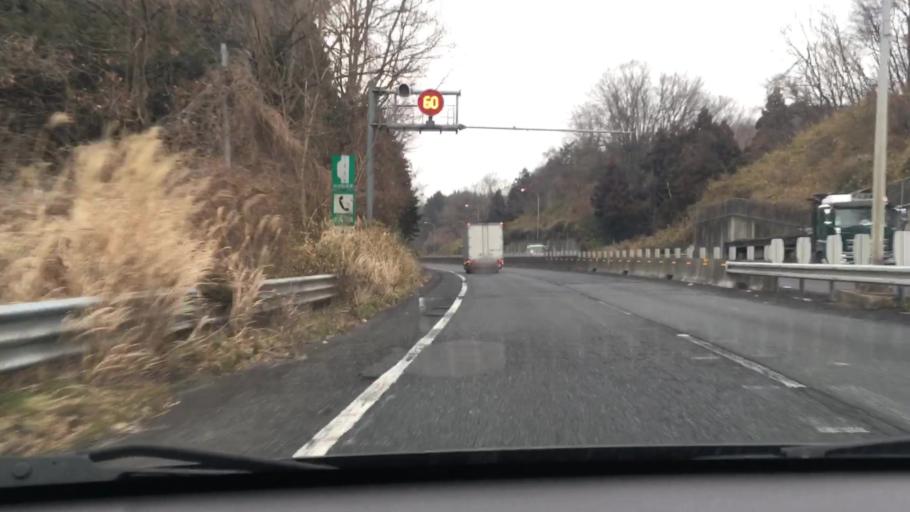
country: JP
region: Mie
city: Nabari
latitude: 34.6849
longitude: 136.0465
